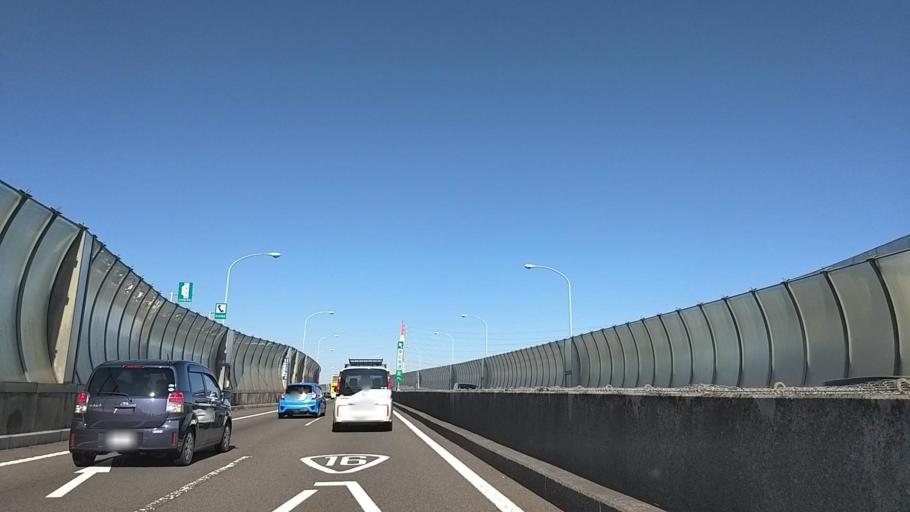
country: JP
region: Kanagawa
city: Minami-rinkan
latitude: 35.5005
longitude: 139.4916
